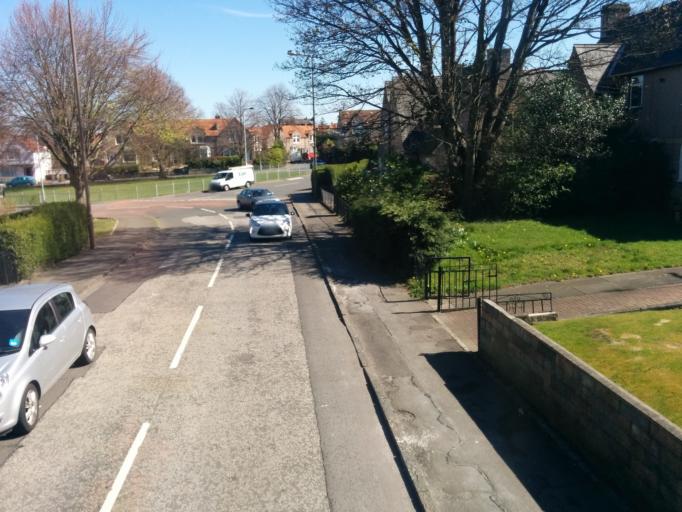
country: GB
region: Scotland
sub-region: Edinburgh
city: Edinburgh
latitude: 55.9761
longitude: -3.2213
